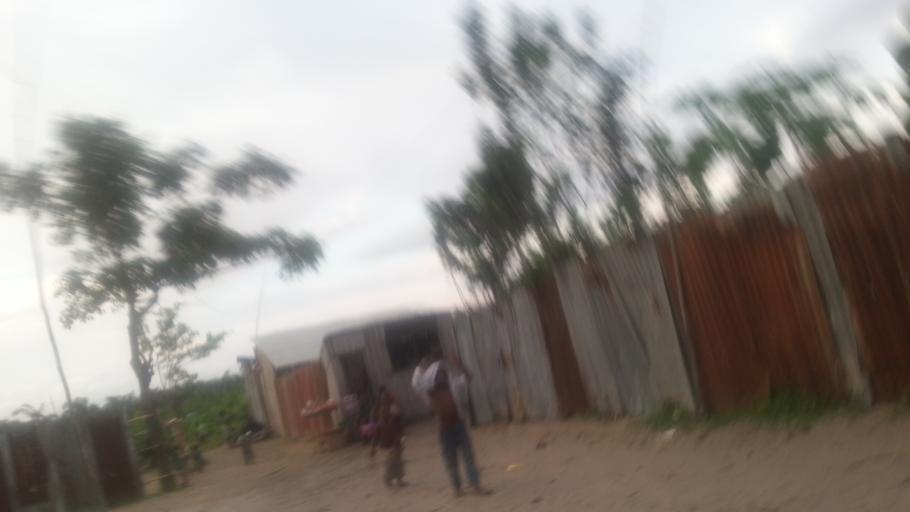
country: BJ
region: Littoral
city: Cotonou
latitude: 6.3868
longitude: 2.5366
